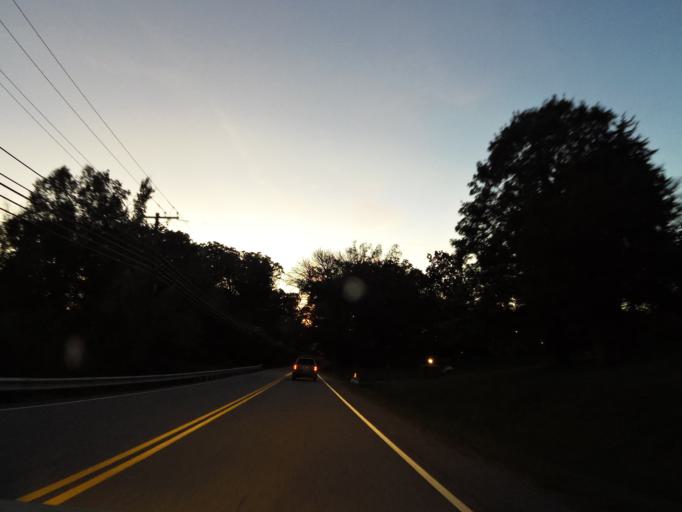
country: US
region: Tennessee
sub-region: Knox County
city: Mascot
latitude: 36.0174
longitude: -83.6804
